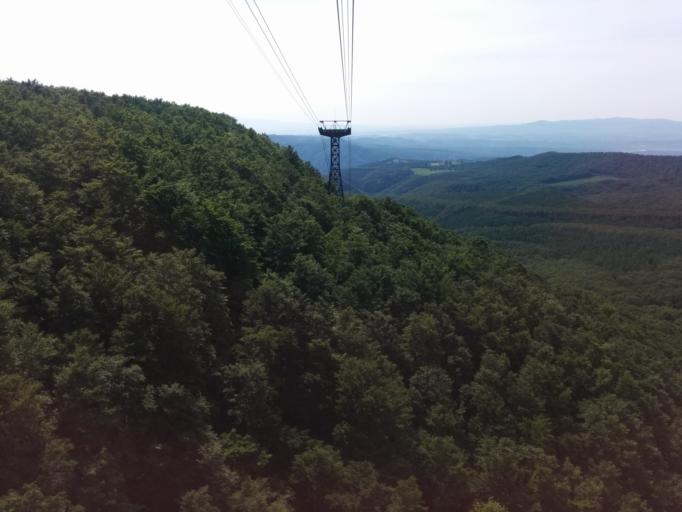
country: JP
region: Aomori
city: Aomori Shi
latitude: 40.6796
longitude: 140.8393
